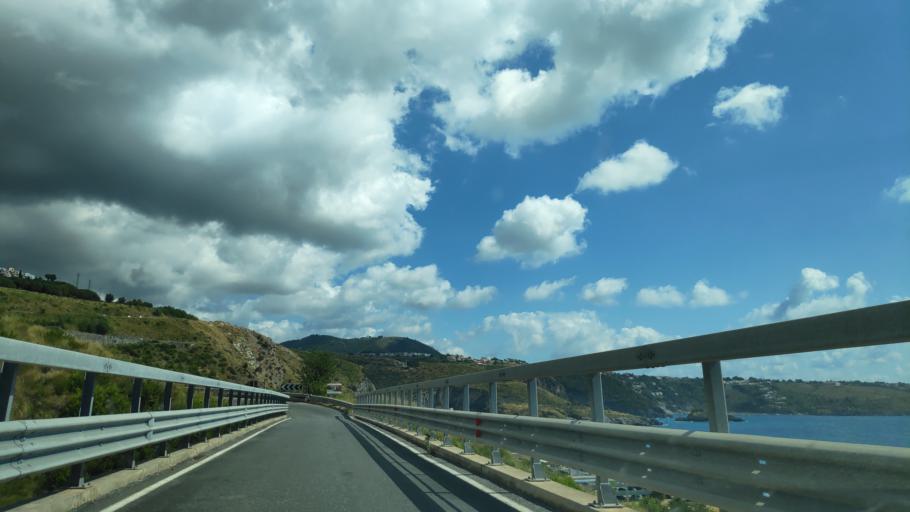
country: IT
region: Calabria
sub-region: Provincia di Cosenza
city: Praia a Mare
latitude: 39.8691
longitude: 15.7909
